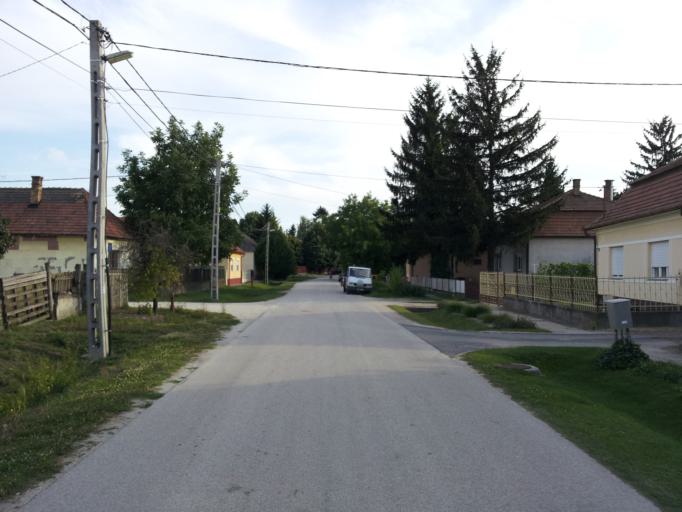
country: HU
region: Pest
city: Kiskunlachaza
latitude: 47.1917
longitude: 19.0120
